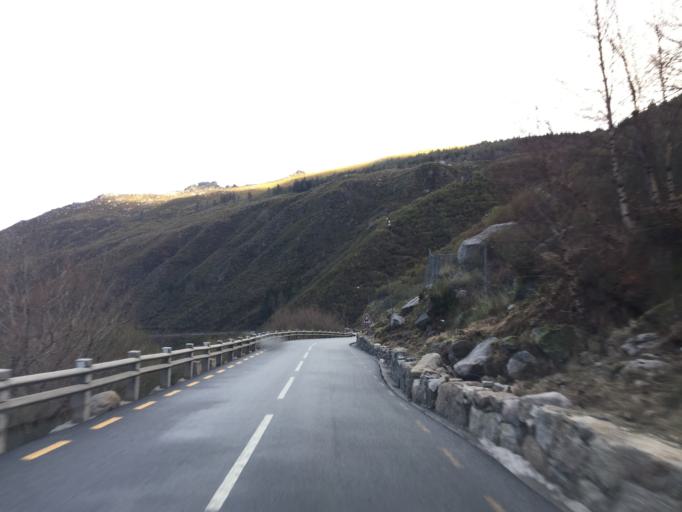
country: PT
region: Castelo Branco
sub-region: Covilha
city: Covilha
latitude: 40.3266
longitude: -7.5796
